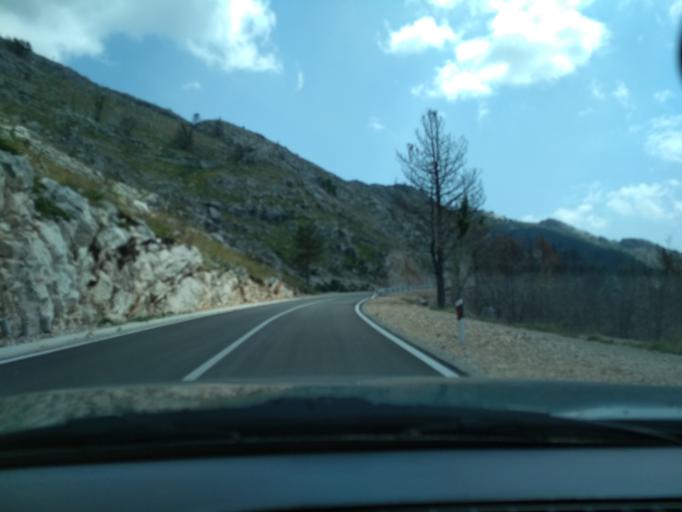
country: ME
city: Dobrota
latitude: 42.4386
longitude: 18.8408
